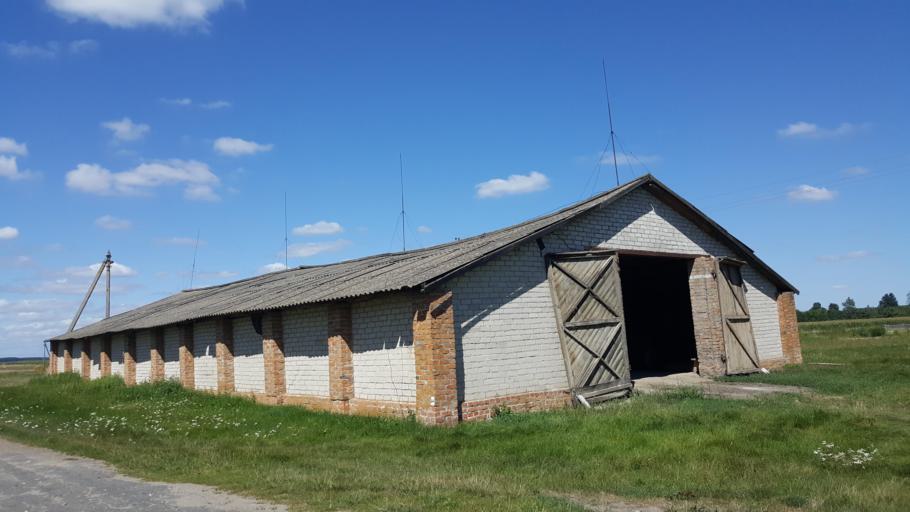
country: BY
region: Brest
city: Kobryn
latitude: 52.2955
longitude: 24.3351
